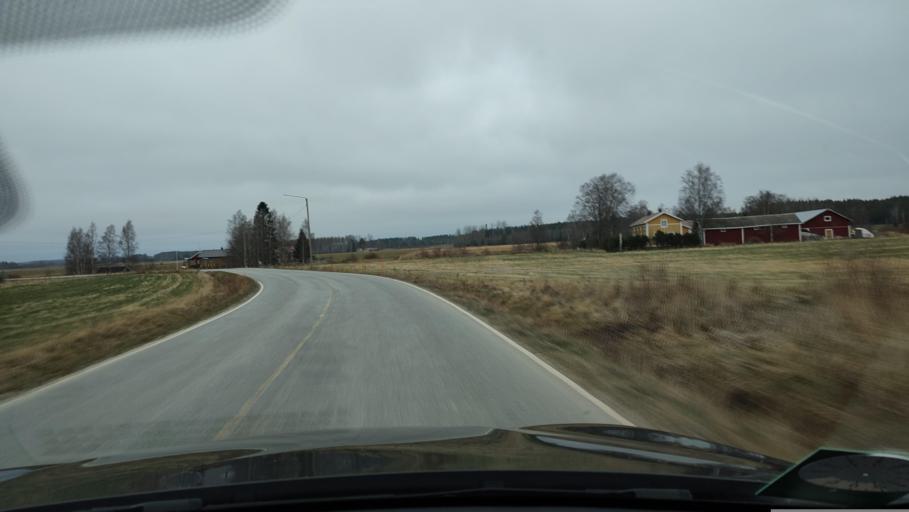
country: FI
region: Southern Ostrobothnia
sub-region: Suupohja
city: Karijoki
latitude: 62.2690
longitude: 21.7250
